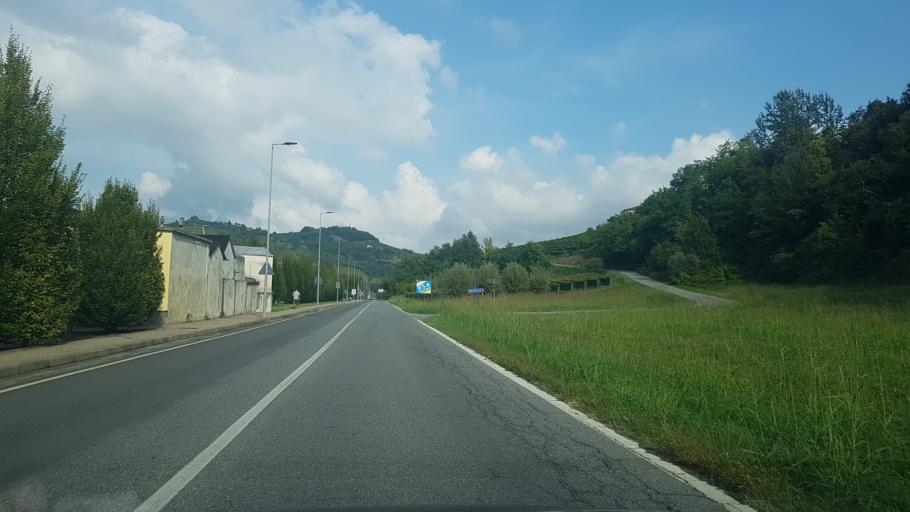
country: IT
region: Piedmont
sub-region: Provincia di Cuneo
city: Santo Stefano Belbo
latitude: 44.7095
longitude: 8.2353
